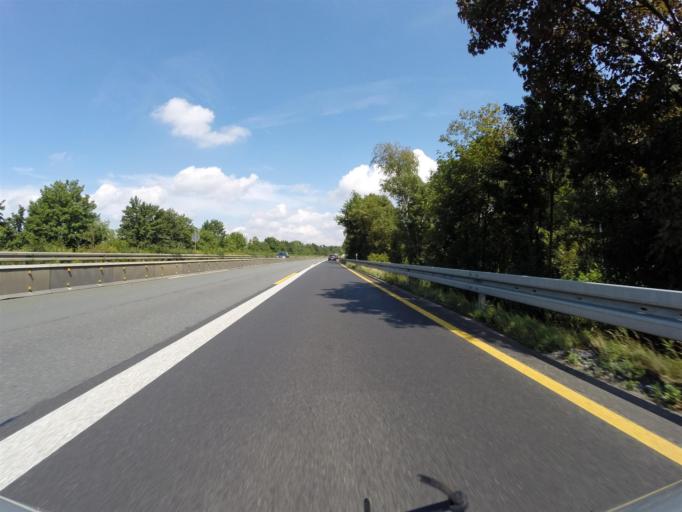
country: DE
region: North Rhine-Westphalia
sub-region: Regierungsbezirk Detmold
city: Hovelhof
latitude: 51.8044
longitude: 8.6991
